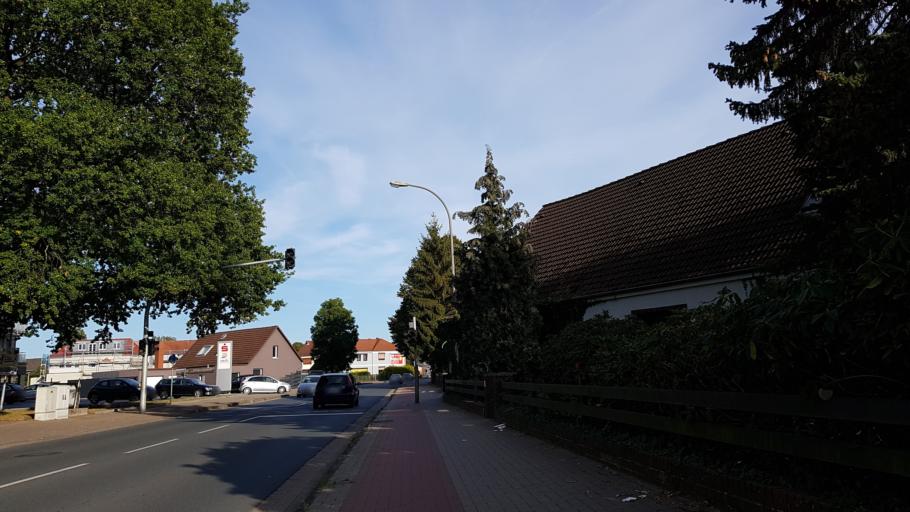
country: DE
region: Lower Saxony
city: Oyten
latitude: 53.0293
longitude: 8.9684
